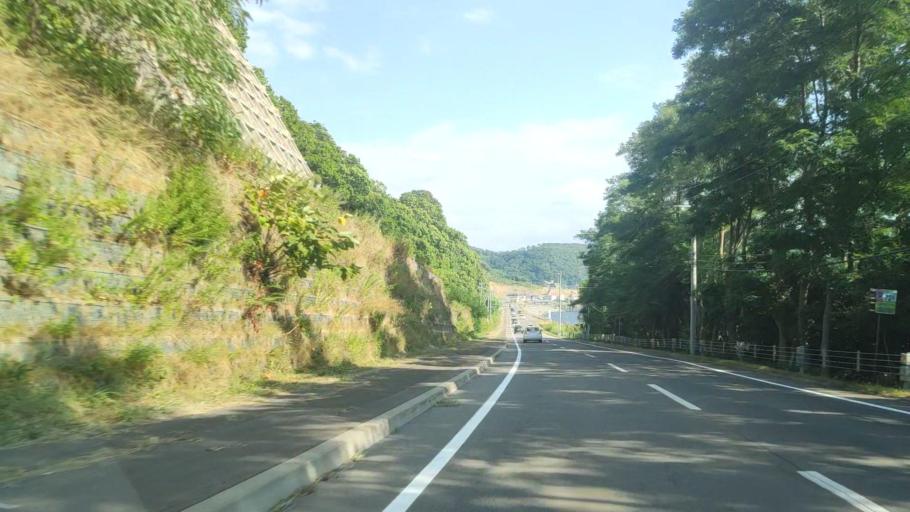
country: JP
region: Hokkaido
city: Ishikari
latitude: 43.6104
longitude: 141.3768
